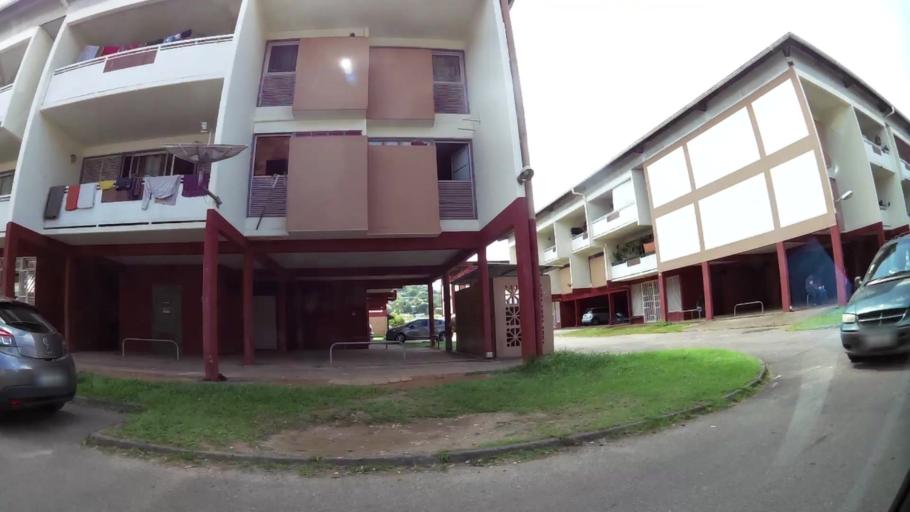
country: GF
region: Guyane
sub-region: Guyane
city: Cayenne
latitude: 4.9212
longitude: -52.3163
